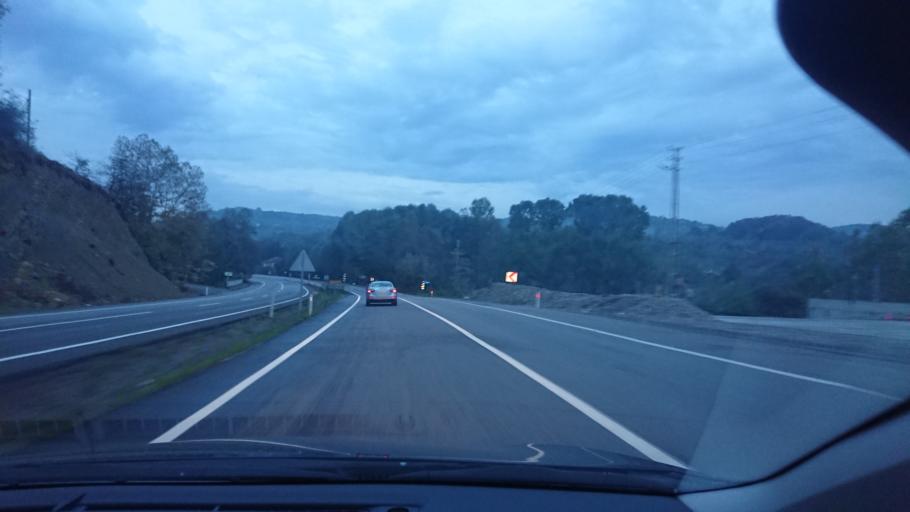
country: TR
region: Zonguldak
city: Beycuma
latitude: 41.3240
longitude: 32.0497
